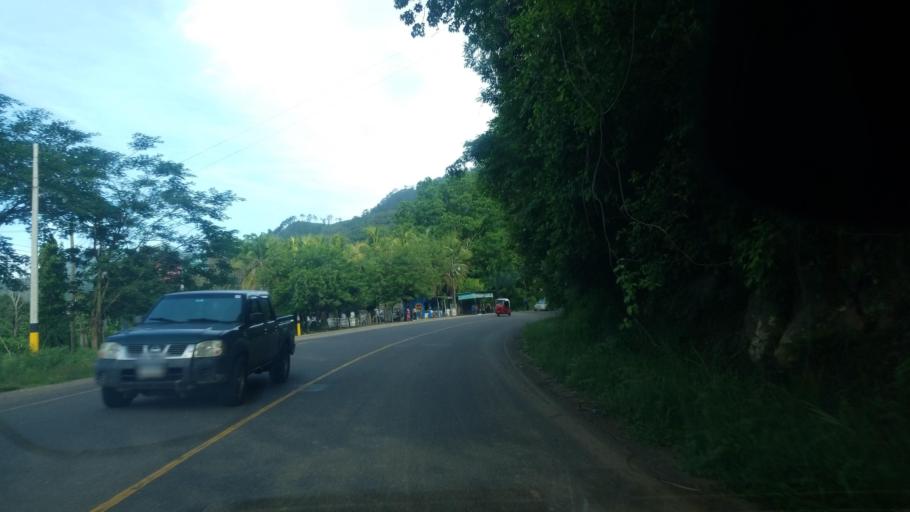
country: HN
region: Santa Barbara
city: Trinidad
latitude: 15.1210
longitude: -88.2015
